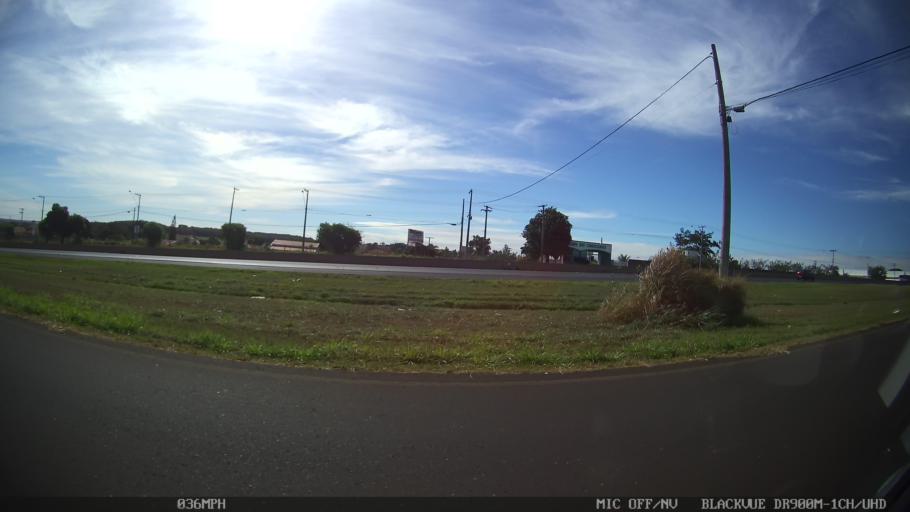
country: BR
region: Sao Paulo
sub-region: Sao Jose Do Rio Preto
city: Sao Jose do Rio Preto
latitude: -20.7947
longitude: -49.3118
